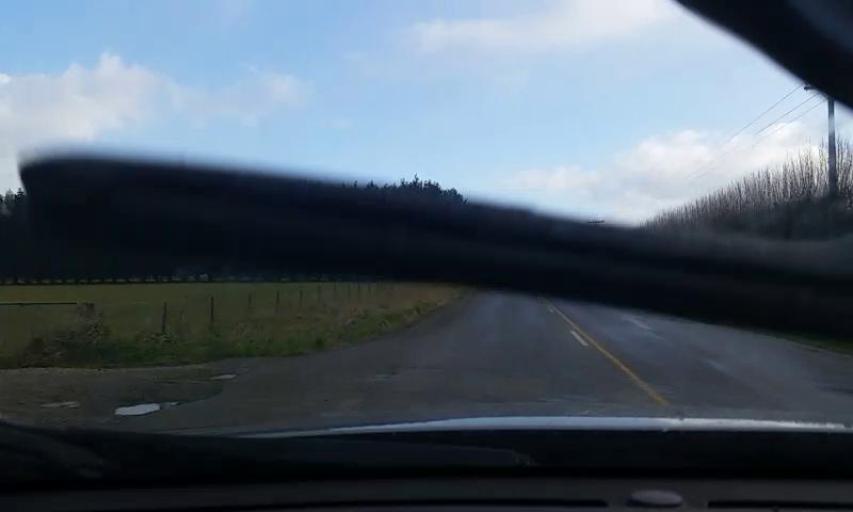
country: NZ
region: Southland
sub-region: Invercargill City
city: Invercargill
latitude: -46.3581
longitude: 168.3401
